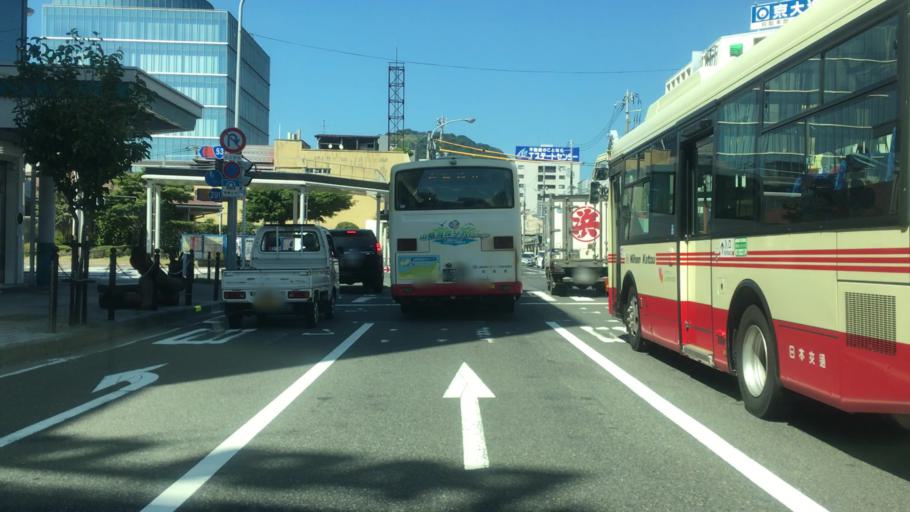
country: JP
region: Tottori
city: Tottori
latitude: 35.4958
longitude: 134.2280
